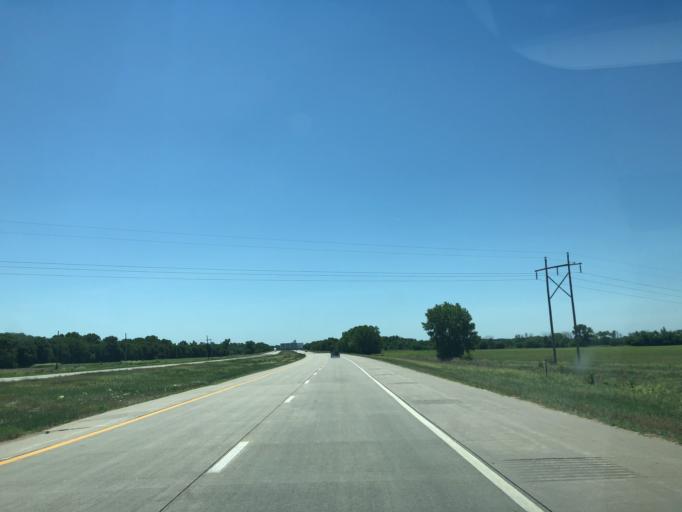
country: US
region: Kansas
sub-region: Cloud County
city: Concordia
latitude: 39.5993
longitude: -97.6600
